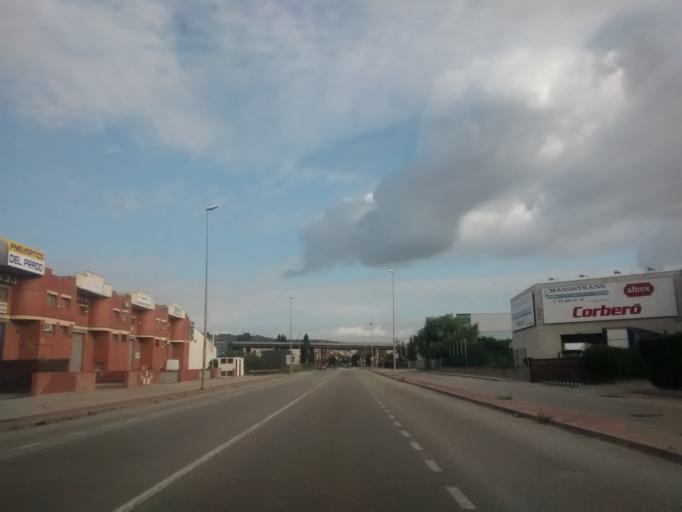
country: ES
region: Catalonia
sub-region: Provincia de Barcelona
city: Palleja
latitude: 41.4120
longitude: 2.0014
